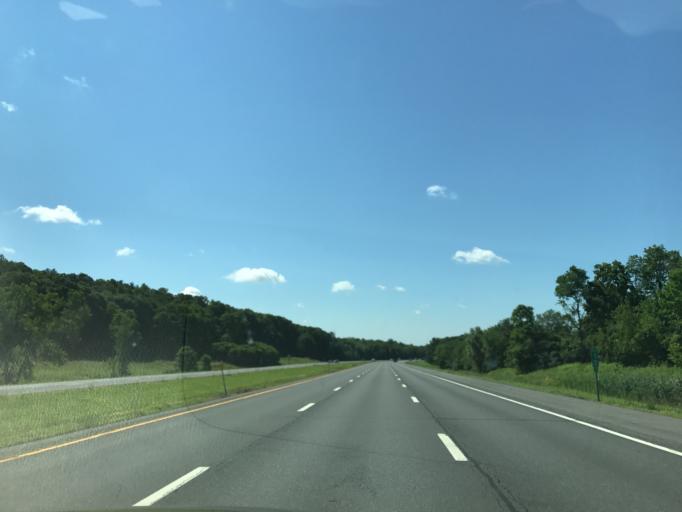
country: US
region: New York
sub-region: Rensselaer County
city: East Greenbush
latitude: 42.5961
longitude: -73.6795
